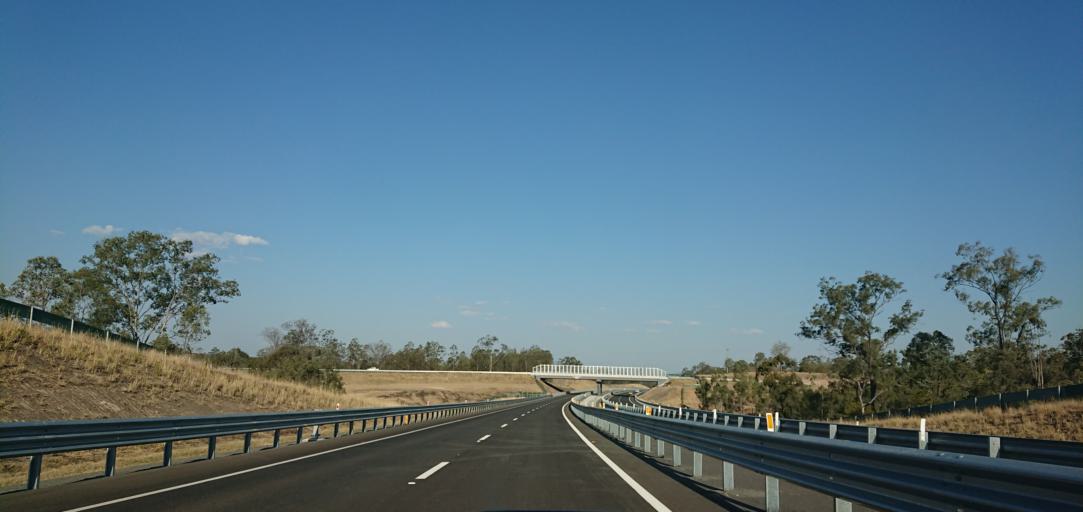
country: AU
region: Queensland
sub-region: Toowoomba
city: East Toowoomba
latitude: -27.5229
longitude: 152.0627
